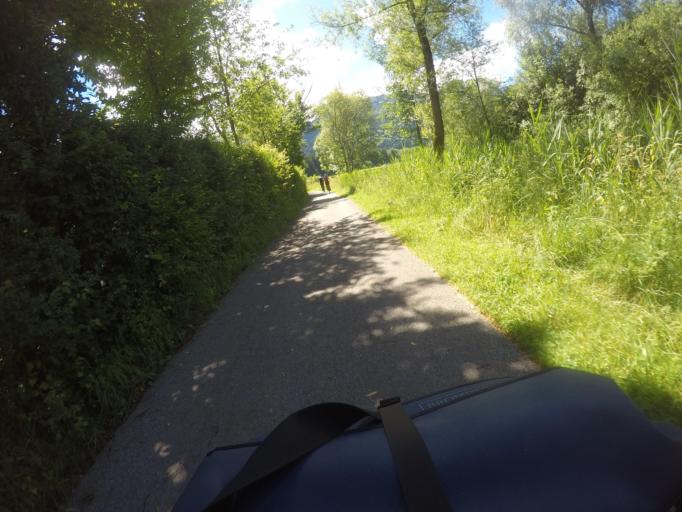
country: DE
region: Bavaria
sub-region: Swabia
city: Schwangau
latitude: 47.5905
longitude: 10.7661
